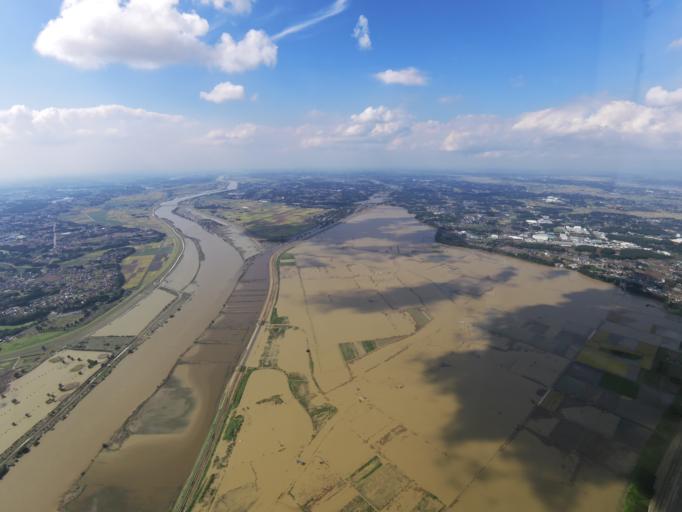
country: JP
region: Ibaraki
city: Moriya
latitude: 35.9508
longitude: 139.9393
